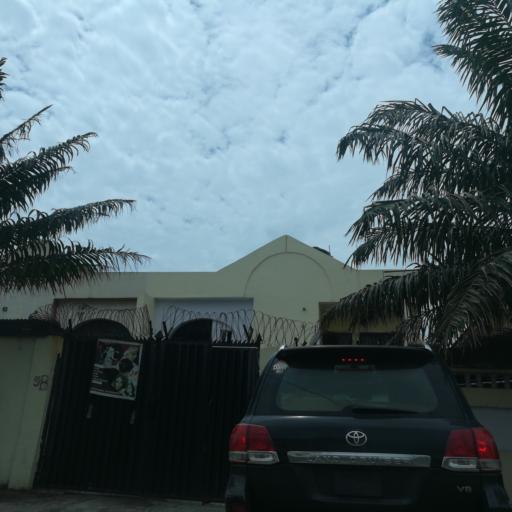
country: NG
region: Lagos
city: Ikoyi
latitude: 6.4439
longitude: 3.4615
